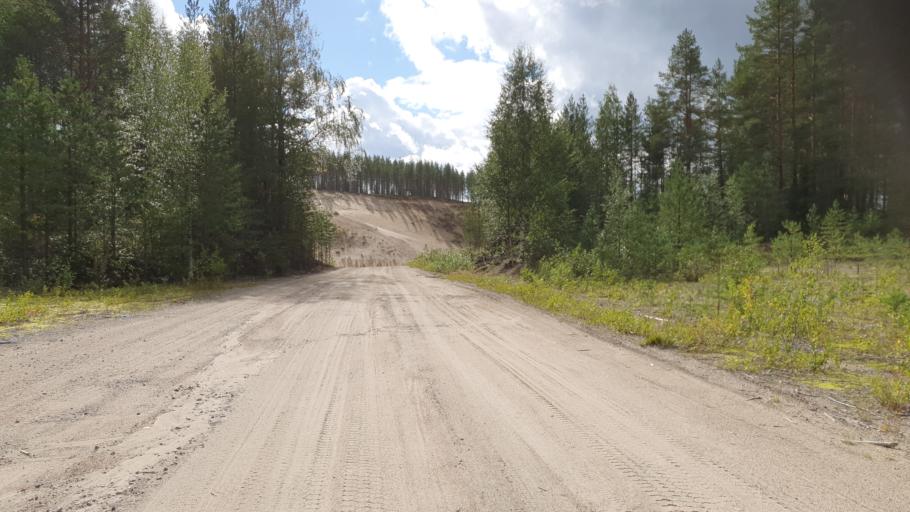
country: FI
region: Kainuu
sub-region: Kehys-Kainuu
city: Kuhmo
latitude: 64.1537
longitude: 29.3783
